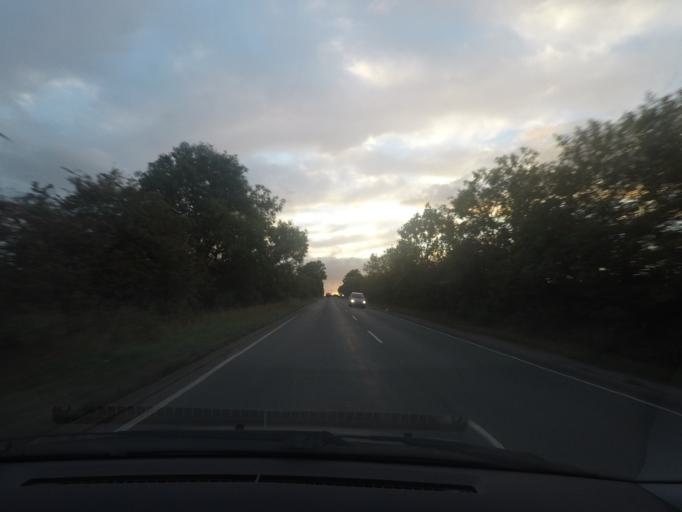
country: GB
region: England
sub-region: North Lincolnshire
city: Barnetby le Wold
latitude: 53.5824
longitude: -0.3991
